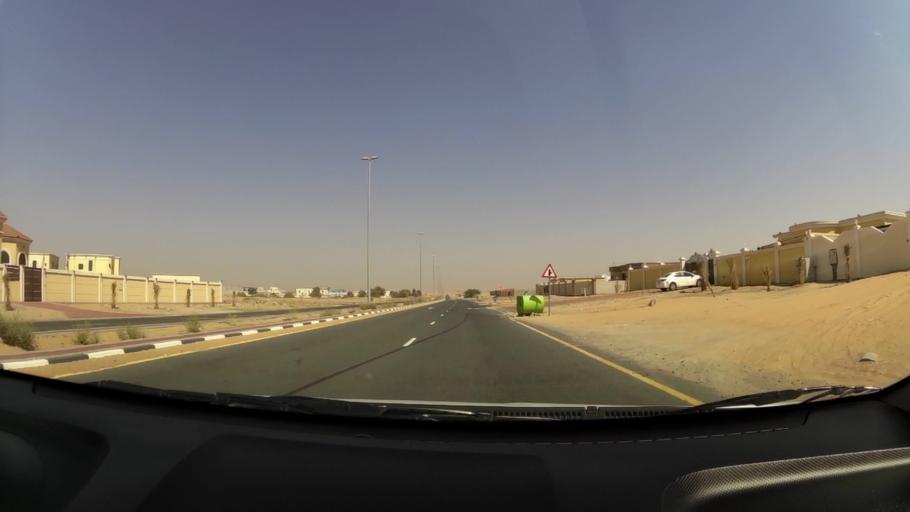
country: AE
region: Umm al Qaywayn
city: Umm al Qaywayn
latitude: 25.4747
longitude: 55.6069
